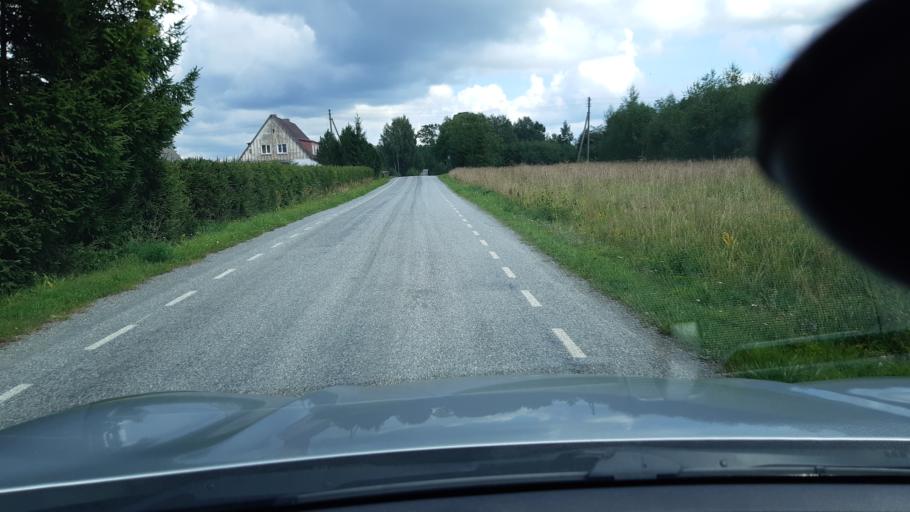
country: EE
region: Raplamaa
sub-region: Kehtna vald
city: Kehtna
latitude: 58.9057
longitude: 25.0342
